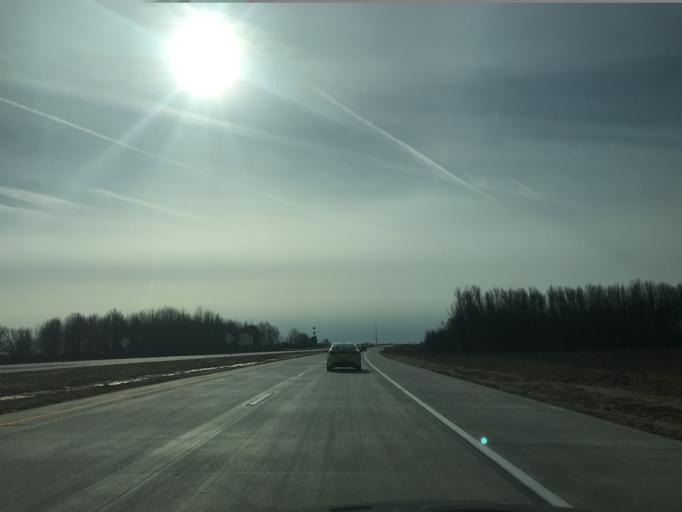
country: US
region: Delaware
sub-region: New Castle County
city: Middletown
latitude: 39.5128
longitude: -75.6918
